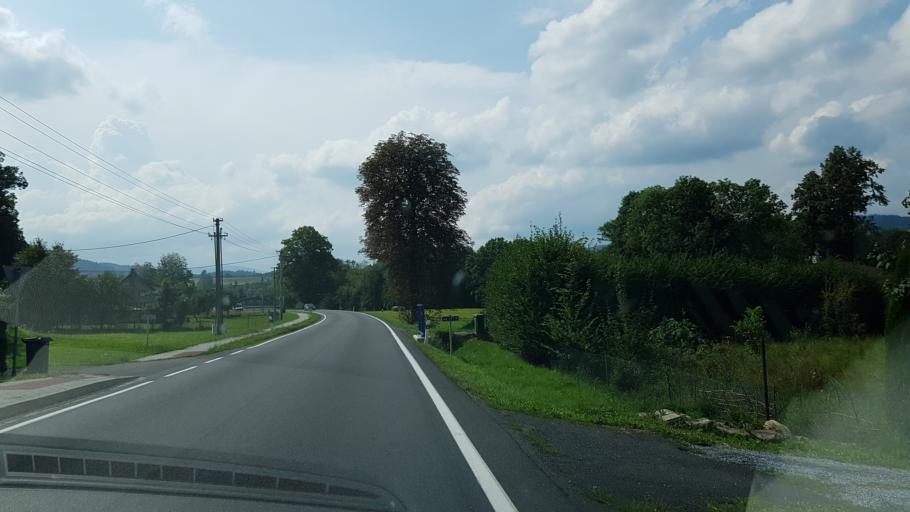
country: CZ
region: Olomoucky
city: Pisecna
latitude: 50.2814
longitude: 17.2882
